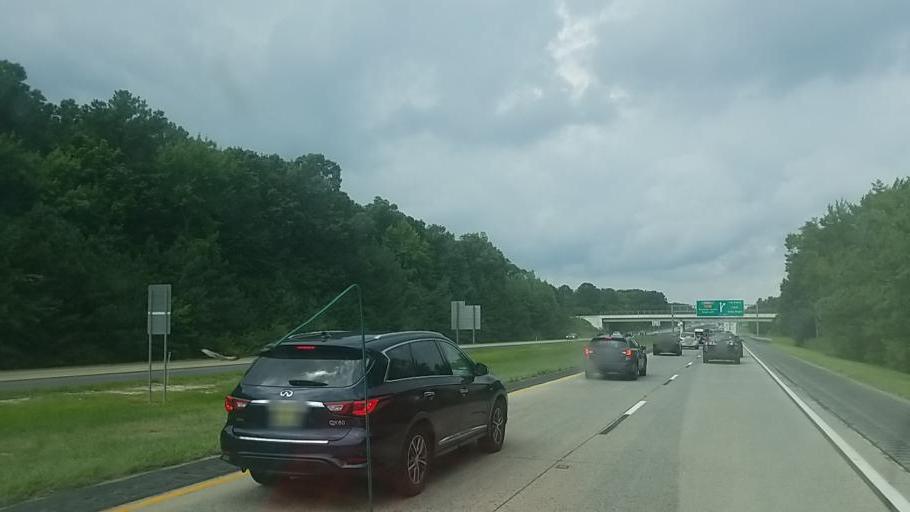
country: US
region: Delaware
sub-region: Kent County
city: Dover
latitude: 39.1752
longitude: -75.5000
